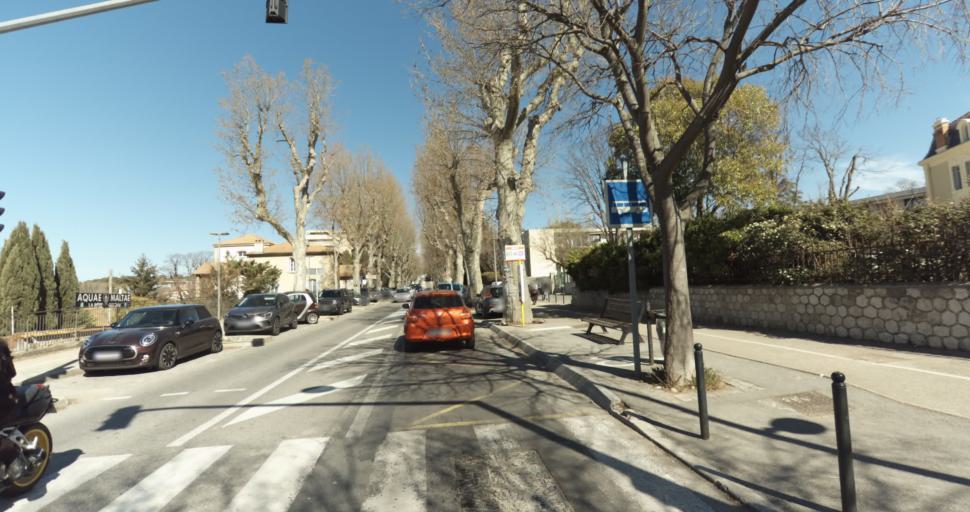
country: FR
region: Provence-Alpes-Cote d'Azur
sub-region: Departement des Bouches-du-Rhone
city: Aix-en-Provence
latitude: 43.5348
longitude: 5.4360
